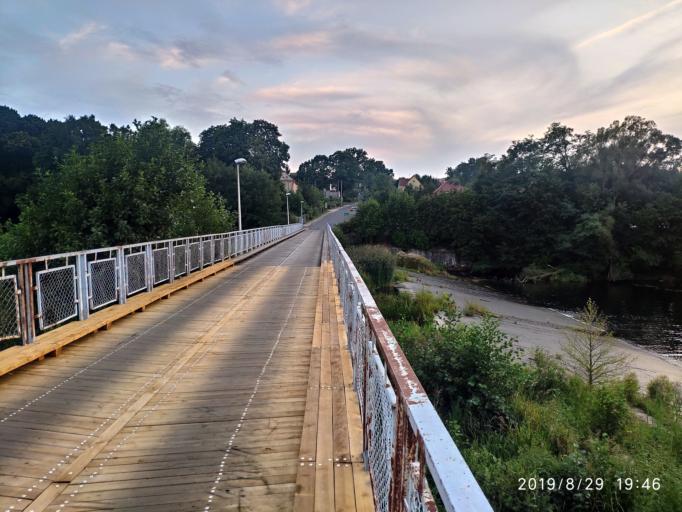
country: PL
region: Lubusz
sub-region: Powiat krosnienski
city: Bobrowice
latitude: 51.9880
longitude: 15.0645
